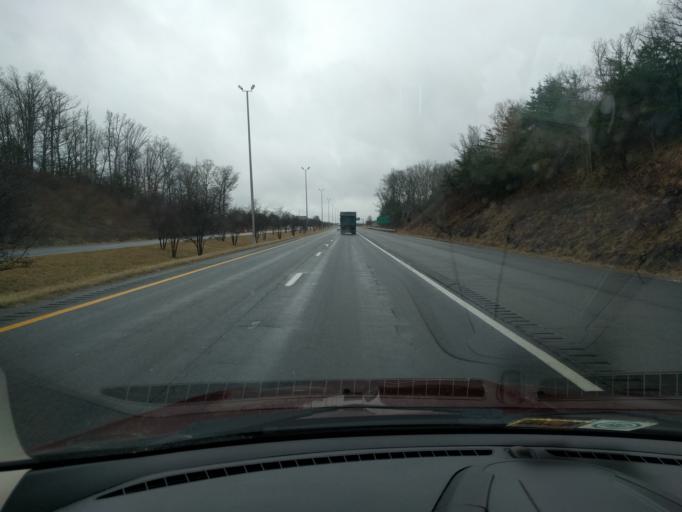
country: US
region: Virginia
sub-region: Montgomery County
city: Merrimac
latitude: 37.1999
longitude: -80.4128
